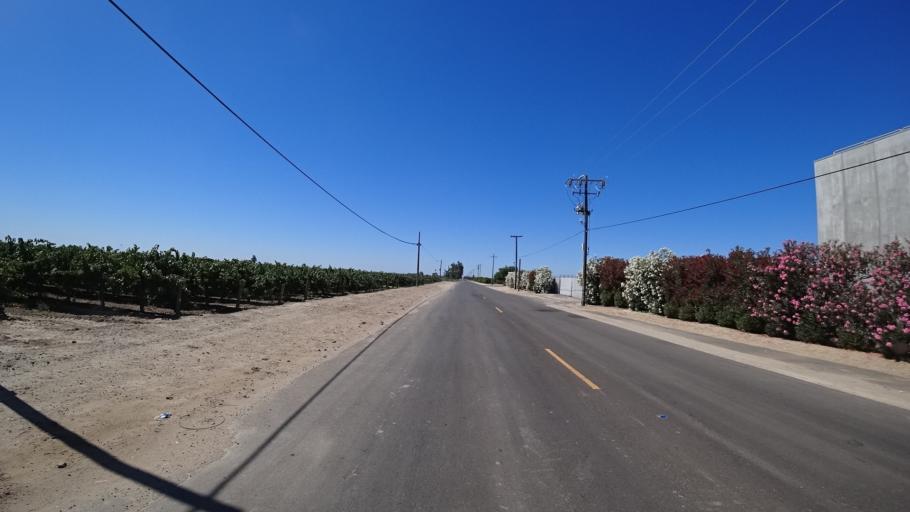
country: US
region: California
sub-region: Fresno County
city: Easton
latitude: 36.6883
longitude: -119.7998
